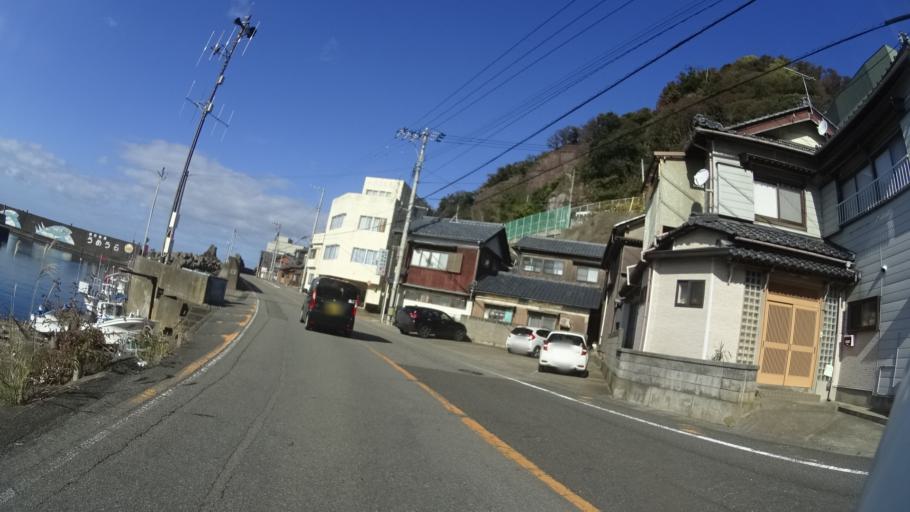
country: JP
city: Asahi
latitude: 35.9557
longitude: 135.9817
